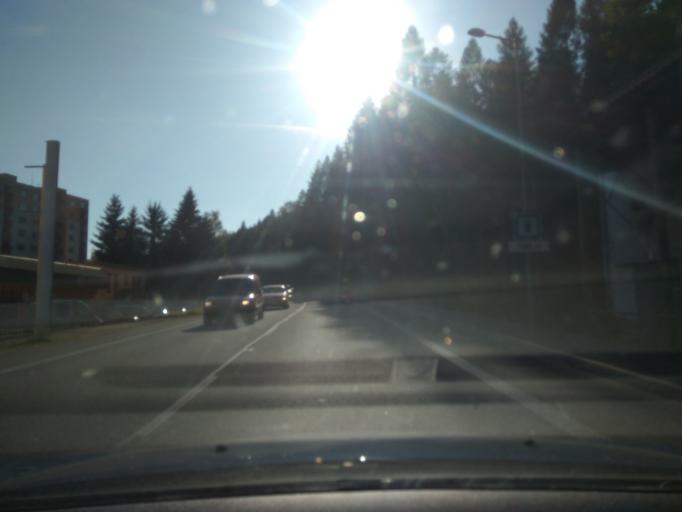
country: SK
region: Nitriansky
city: Handlova
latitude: 48.7412
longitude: 18.7629
